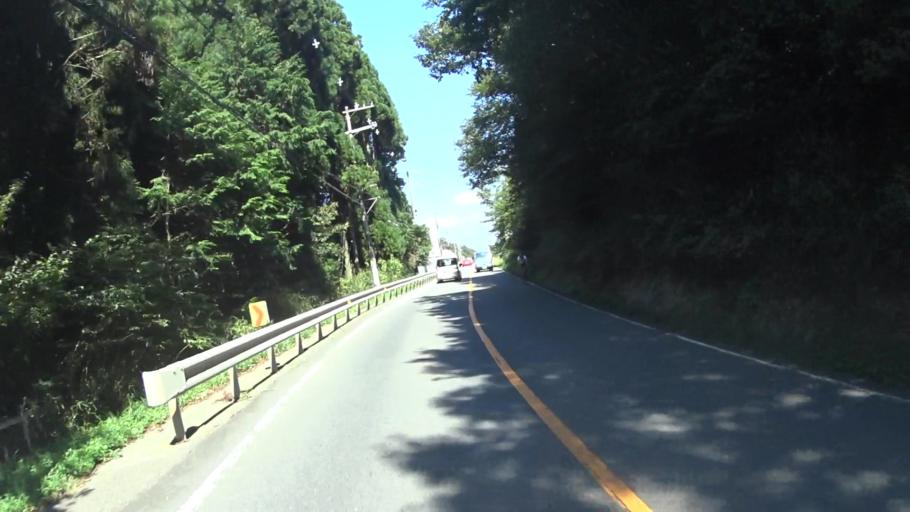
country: JP
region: Kyoto
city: Kameoka
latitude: 34.9499
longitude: 135.4978
